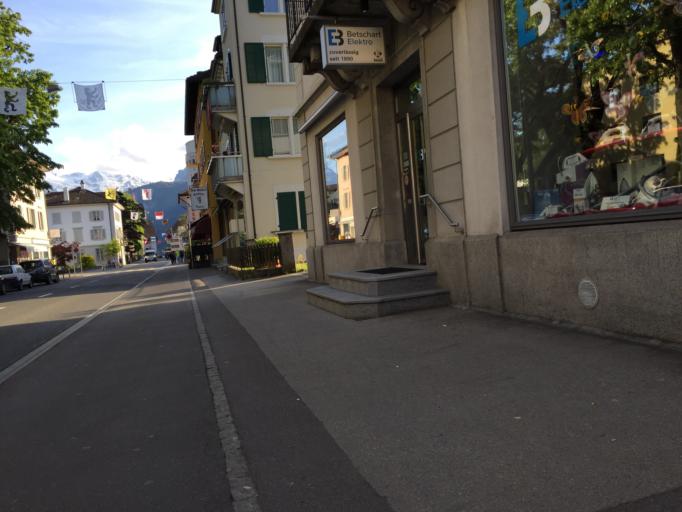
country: CH
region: Schwyz
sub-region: Bezirk Schwyz
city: Ingenbohl
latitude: 46.9962
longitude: 8.6069
